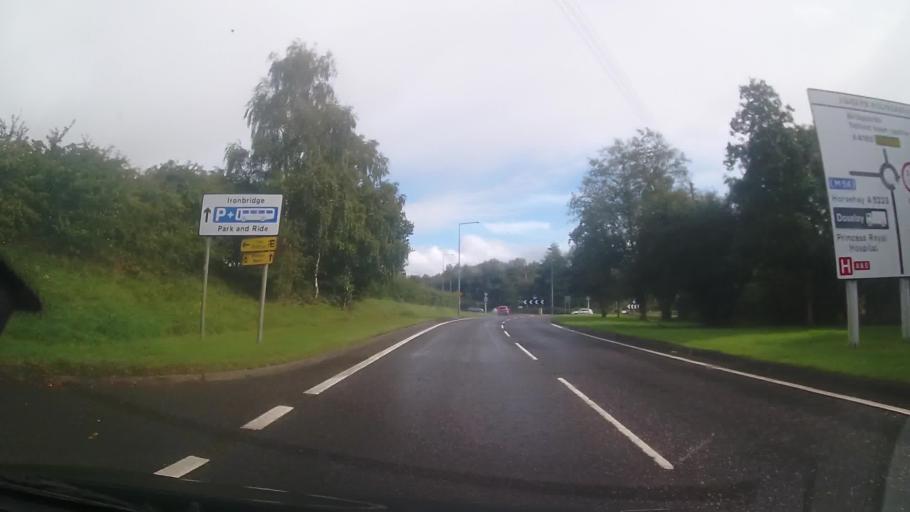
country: GB
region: England
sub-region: Telford and Wrekin
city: Ironbridge
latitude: 52.6523
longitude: -2.4973
